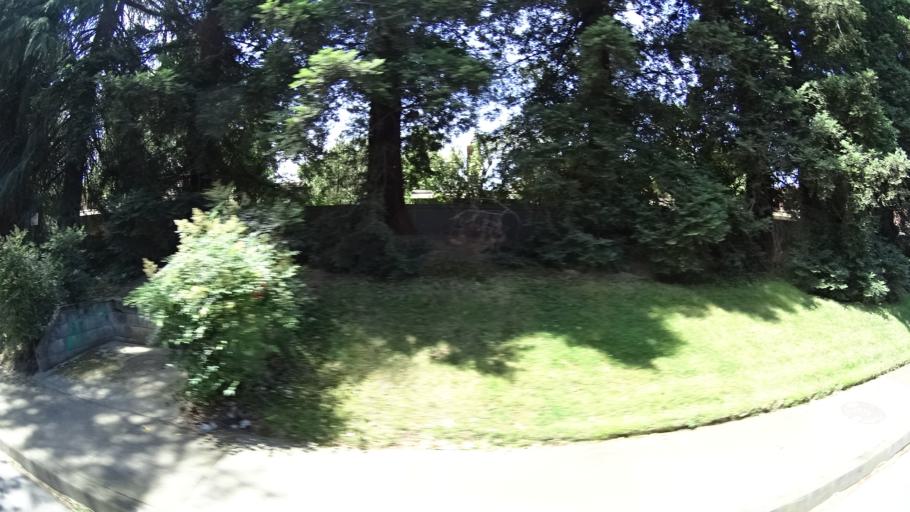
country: US
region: California
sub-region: Sacramento County
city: Arden-Arcade
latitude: 38.5713
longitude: -121.4116
